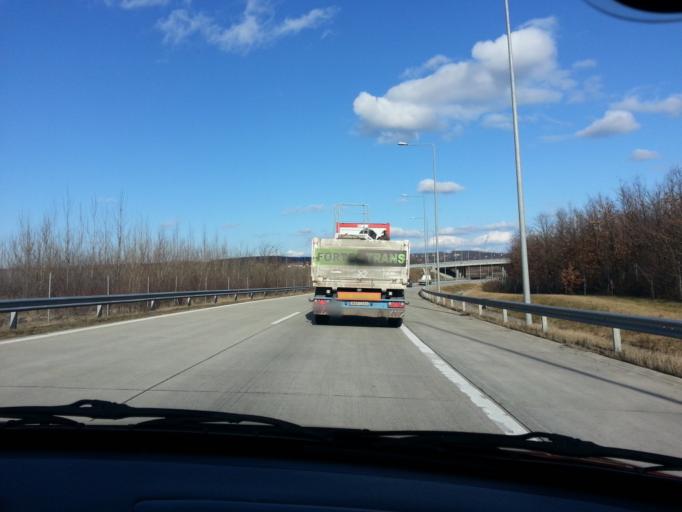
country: HU
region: Pest
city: Szada
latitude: 47.6107
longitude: 19.3193
